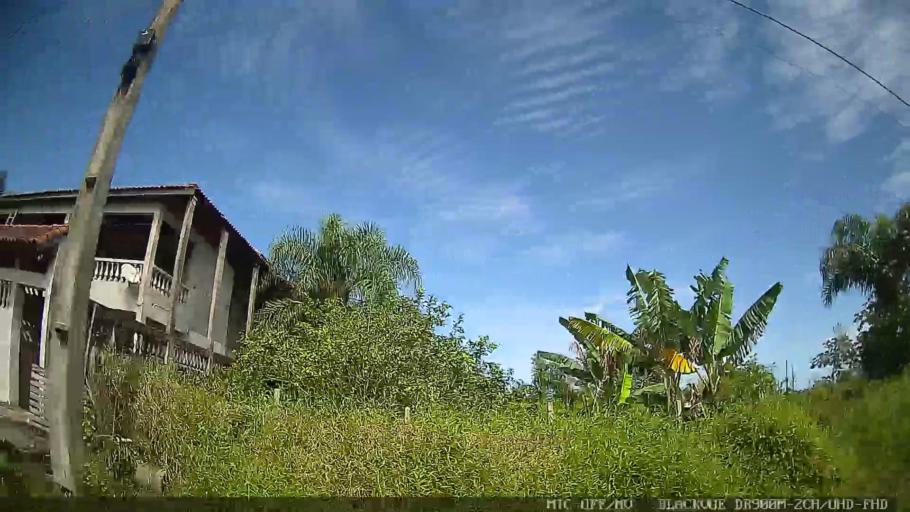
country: BR
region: Sao Paulo
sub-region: Iguape
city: Iguape
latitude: -24.7810
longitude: -47.6071
